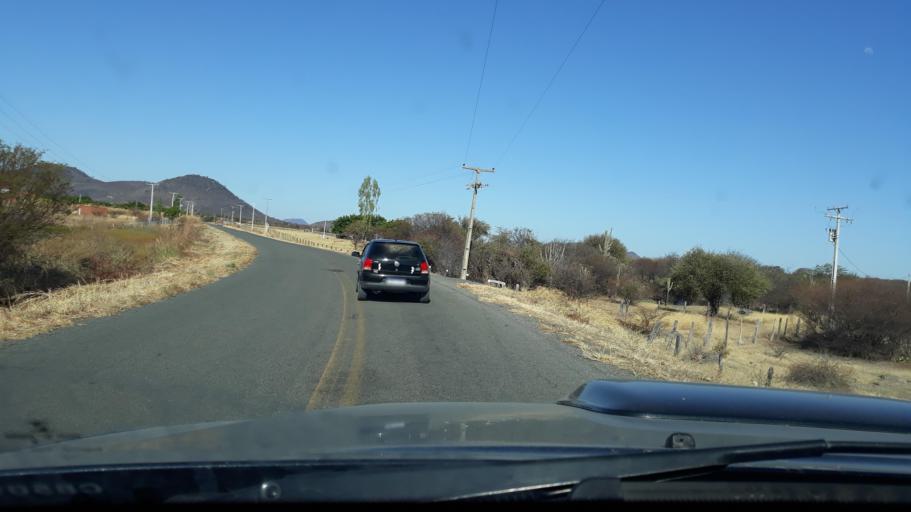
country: BR
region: Bahia
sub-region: Guanambi
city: Guanambi
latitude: -14.0225
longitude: -42.8684
